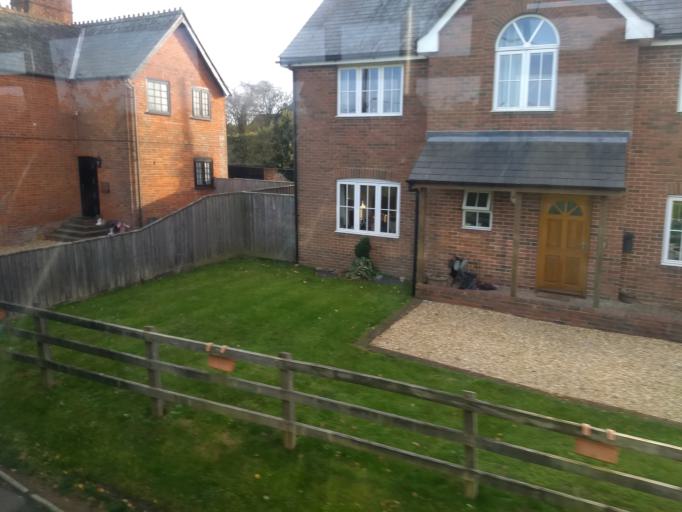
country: GB
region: England
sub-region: Isle of Wight
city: Shalfleet
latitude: 50.7014
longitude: -1.4128
